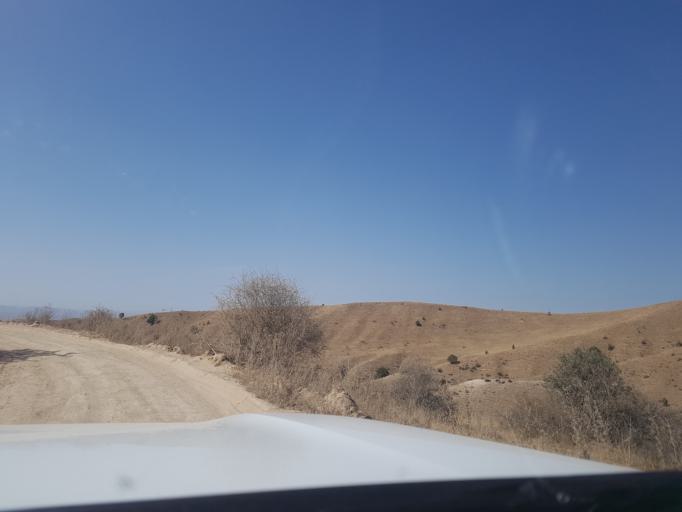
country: TM
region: Ahal
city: Baharly
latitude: 38.2965
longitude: 56.9359
